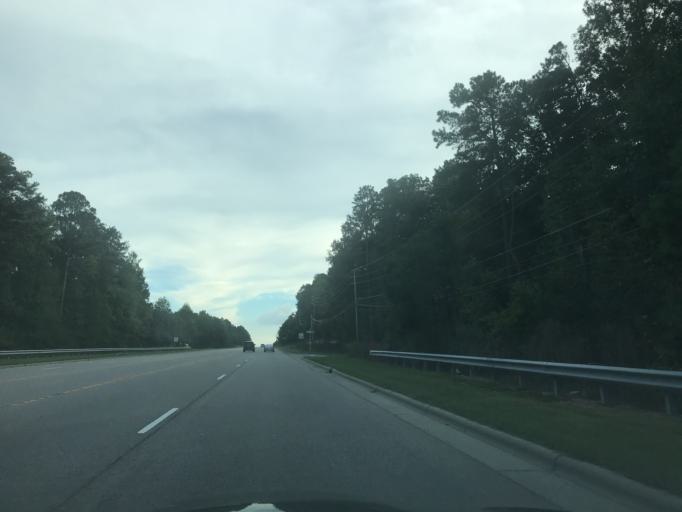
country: US
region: North Carolina
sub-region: Wake County
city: Green Level
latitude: 35.7683
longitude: -78.8743
